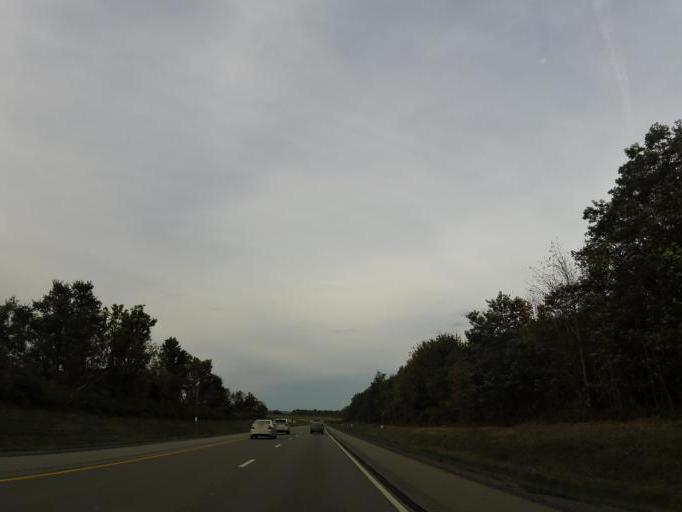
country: US
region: New York
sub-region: Erie County
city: Angola
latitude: 42.6166
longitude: -79.0127
